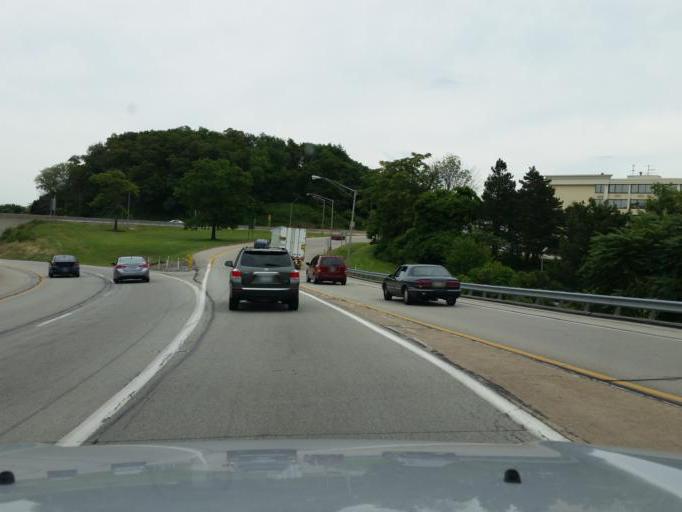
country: US
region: Pennsylvania
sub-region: Allegheny County
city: Monroeville
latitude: 40.4380
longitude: -79.7567
